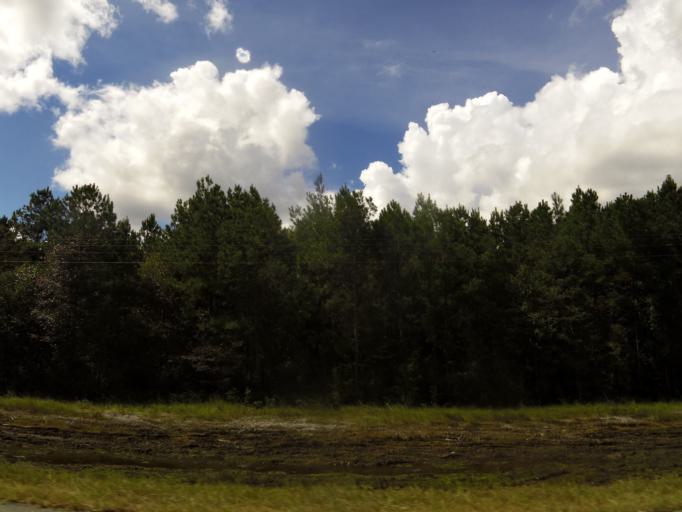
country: US
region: Georgia
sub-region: Brantley County
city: Nahunta
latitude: 31.1125
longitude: -82.0038
